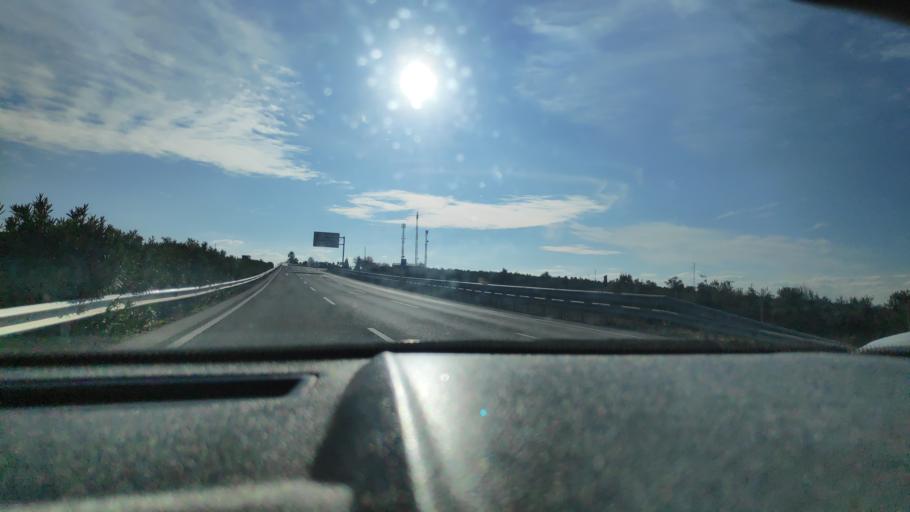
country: ES
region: Andalusia
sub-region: Province of Cordoba
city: La Carlota
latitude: 37.5942
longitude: -4.9780
